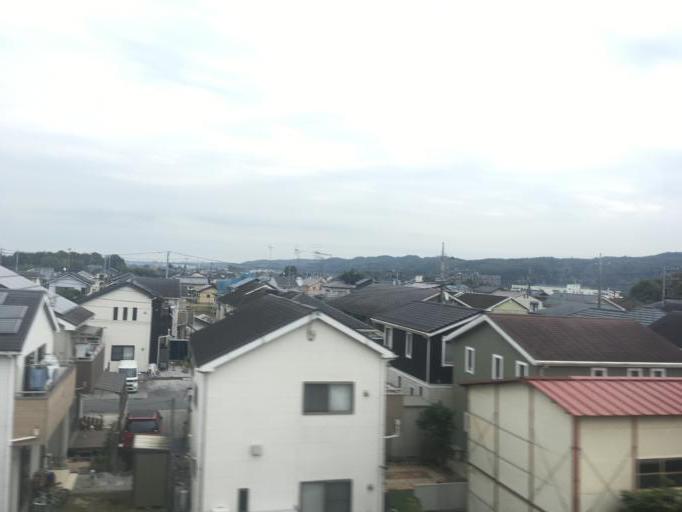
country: JP
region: Saitama
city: Hanno
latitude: 35.8390
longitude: 139.3340
